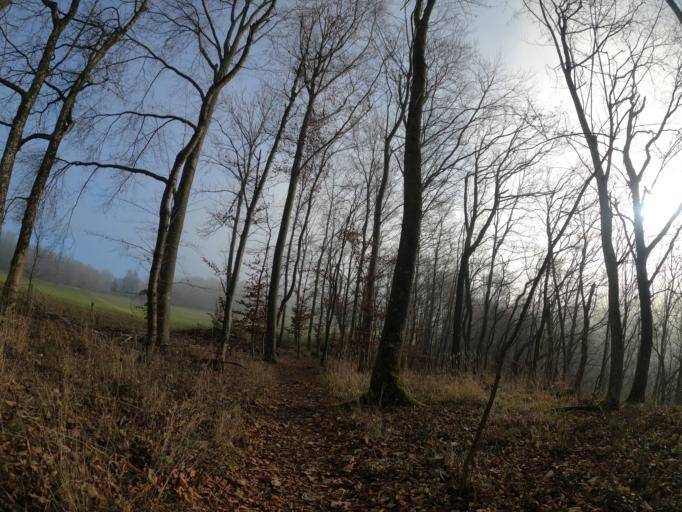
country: DE
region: Baden-Wuerttemberg
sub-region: Regierungsbezirk Stuttgart
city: Deggingen
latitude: 48.5970
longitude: 9.7429
